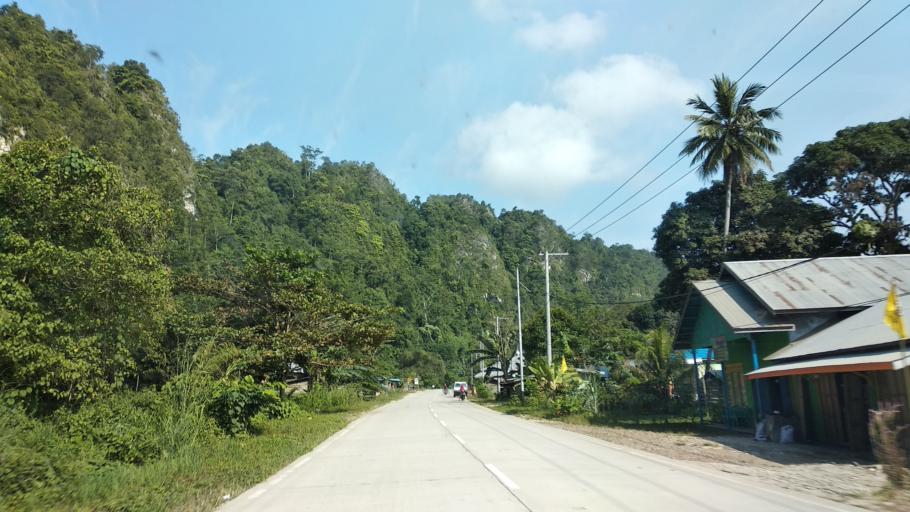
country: ID
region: East Kalimantan
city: Muarakomam
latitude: -1.7016
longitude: 115.8176
